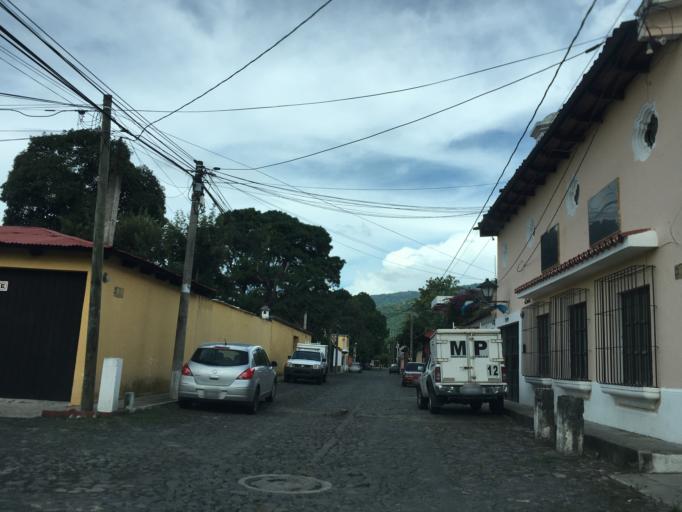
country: GT
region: Sacatepequez
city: Ciudad Vieja
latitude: 14.5423
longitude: -90.7457
